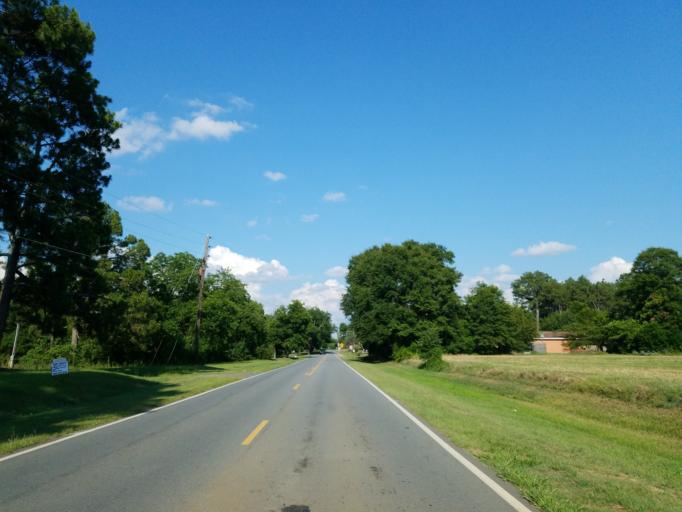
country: US
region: Georgia
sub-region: Dooly County
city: Unadilla
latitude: 32.2604
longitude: -83.7454
